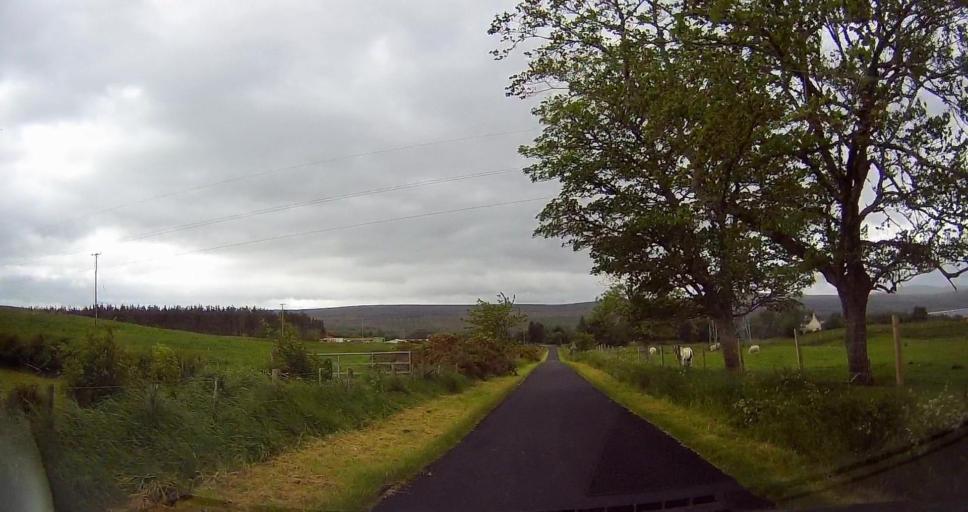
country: GB
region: Scotland
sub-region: Highland
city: Evanton
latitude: 58.0770
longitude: -4.4611
